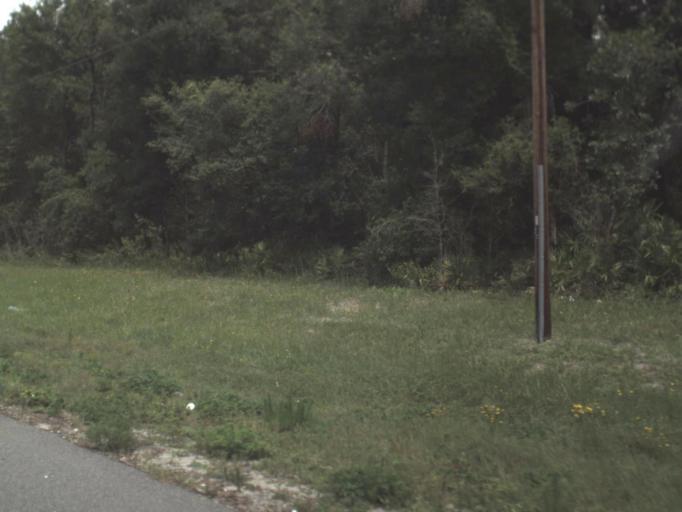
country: US
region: Florida
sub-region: Hernando County
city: Ridge Manor
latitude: 28.5372
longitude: -82.1632
